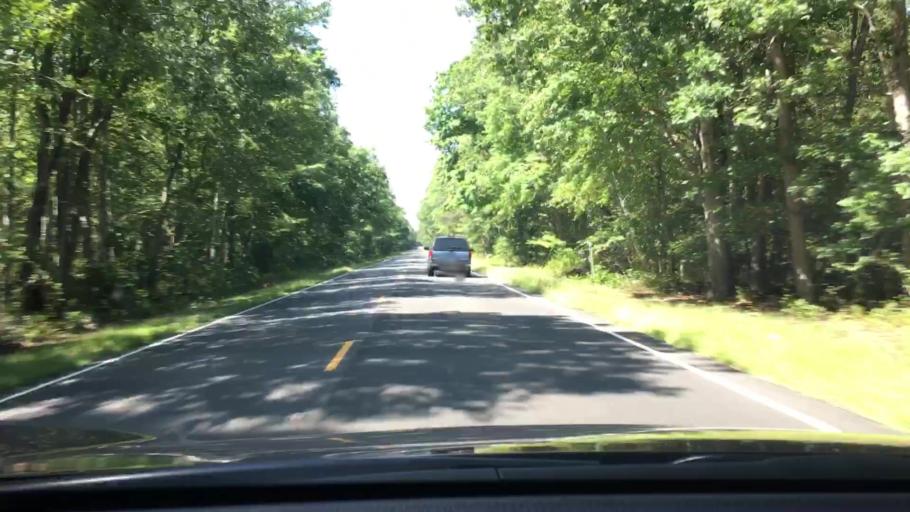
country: US
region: New Jersey
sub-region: Cape May County
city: Woodbine
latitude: 39.2612
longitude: -74.9173
